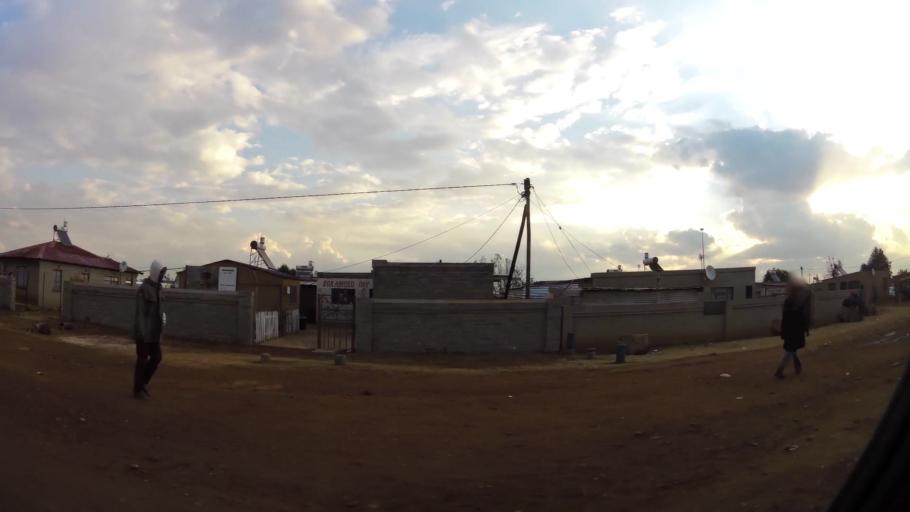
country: ZA
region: Gauteng
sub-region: City of Johannesburg Metropolitan Municipality
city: Orange Farm
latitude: -26.5611
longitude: 27.8326
